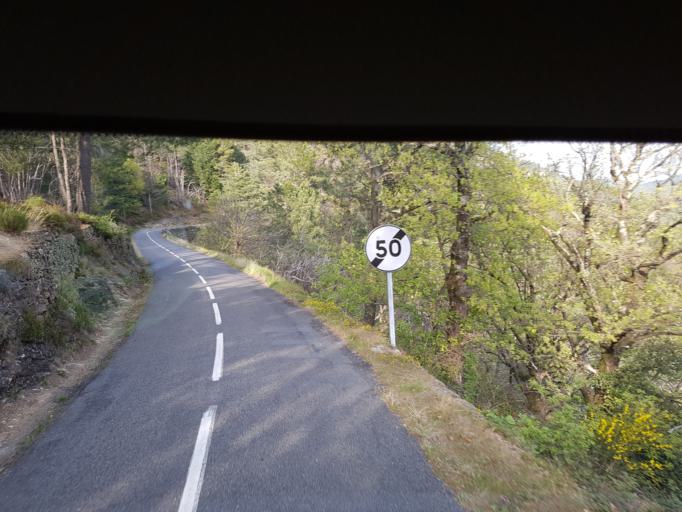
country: FR
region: Languedoc-Roussillon
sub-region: Departement du Gard
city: Branoux-les-Taillades
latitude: 44.3291
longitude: 3.9124
